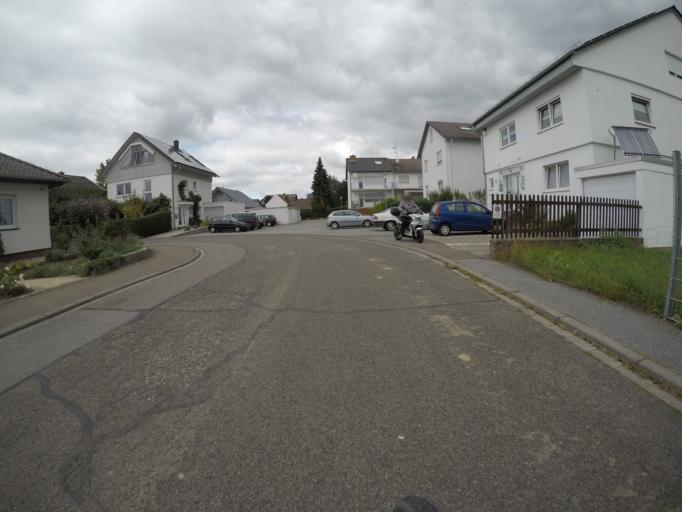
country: DE
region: Baden-Wuerttemberg
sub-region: Karlsruhe Region
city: Laudenbach
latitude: 49.6142
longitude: 8.6517
